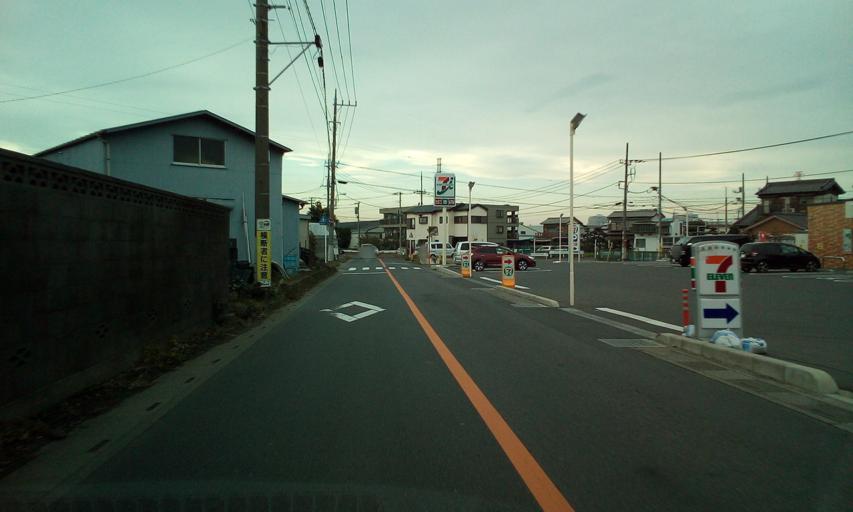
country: JP
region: Chiba
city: Nagareyama
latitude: 35.8427
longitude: 139.8795
